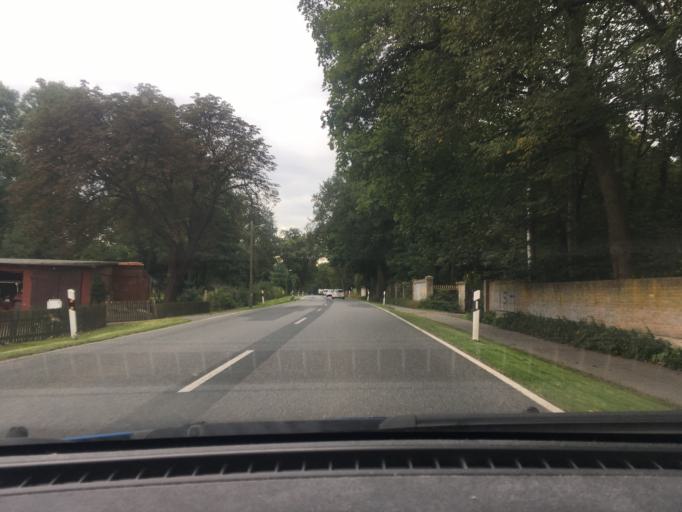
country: DE
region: Lower Saxony
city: Unterluss
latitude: 52.7800
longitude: 10.3411
